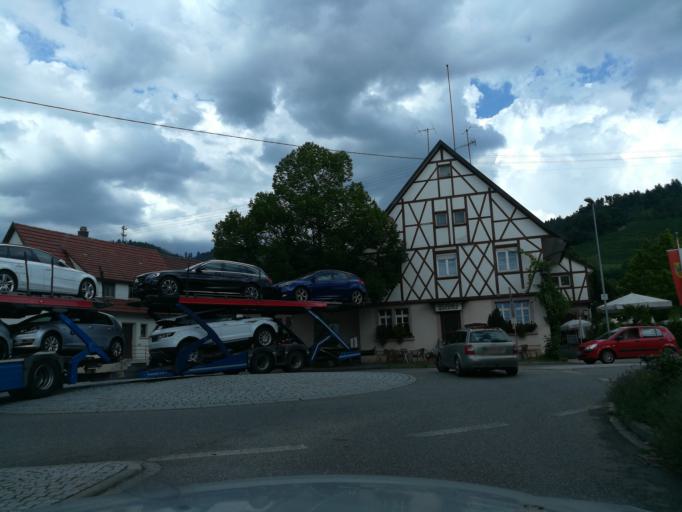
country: DE
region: Baden-Wuerttemberg
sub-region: Freiburg Region
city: Ortenberg
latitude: 48.4473
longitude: 7.9712
